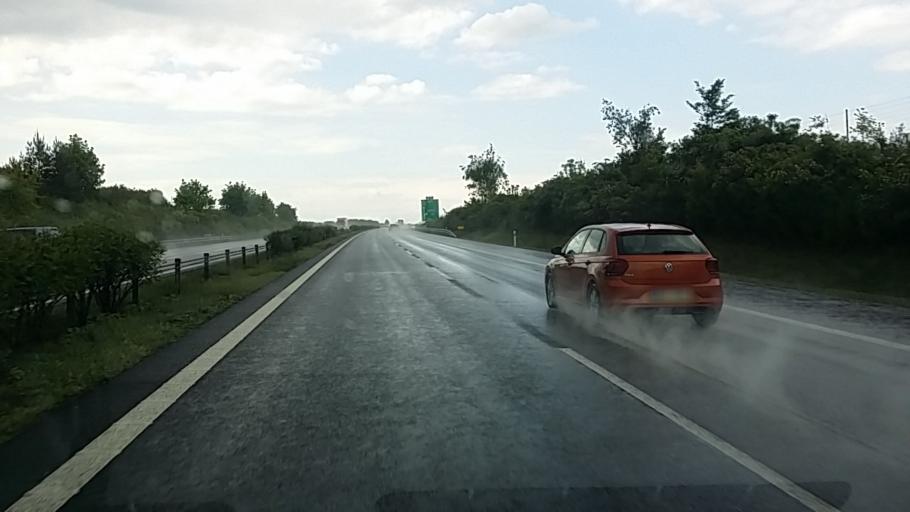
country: CZ
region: Ustecky
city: Roudnice nad Labem
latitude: 50.3892
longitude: 14.2346
